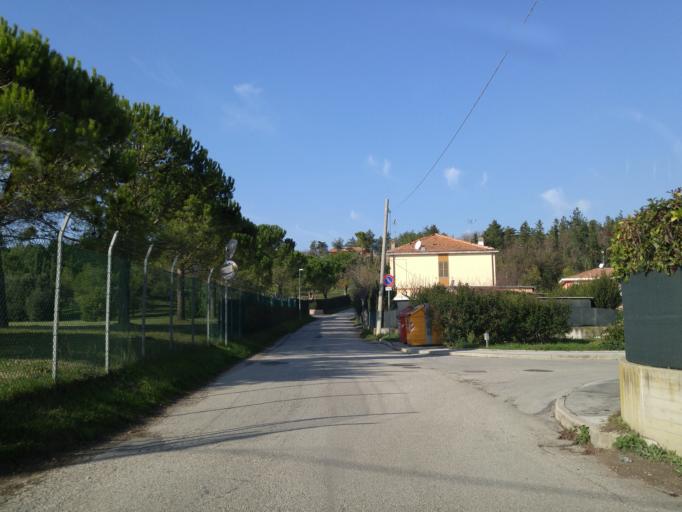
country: IT
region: The Marches
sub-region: Provincia di Pesaro e Urbino
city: Lucrezia
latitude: 43.7810
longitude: 12.9403
